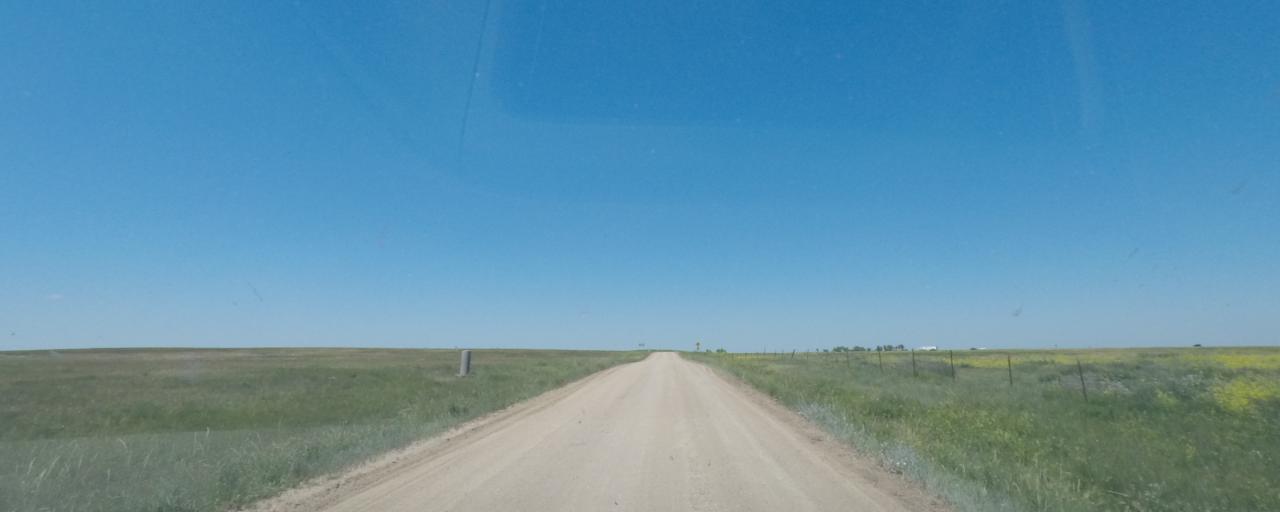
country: US
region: South Dakota
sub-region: Haakon County
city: Philip
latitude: 43.9337
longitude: -102.1587
